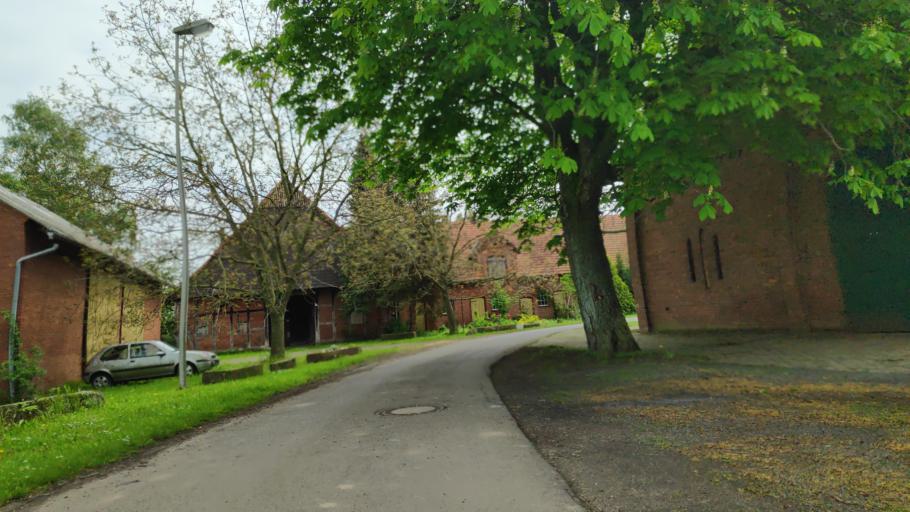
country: DE
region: North Rhine-Westphalia
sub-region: Regierungsbezirk Detmold
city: Petershagen
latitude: 52.3145
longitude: 8.9929
